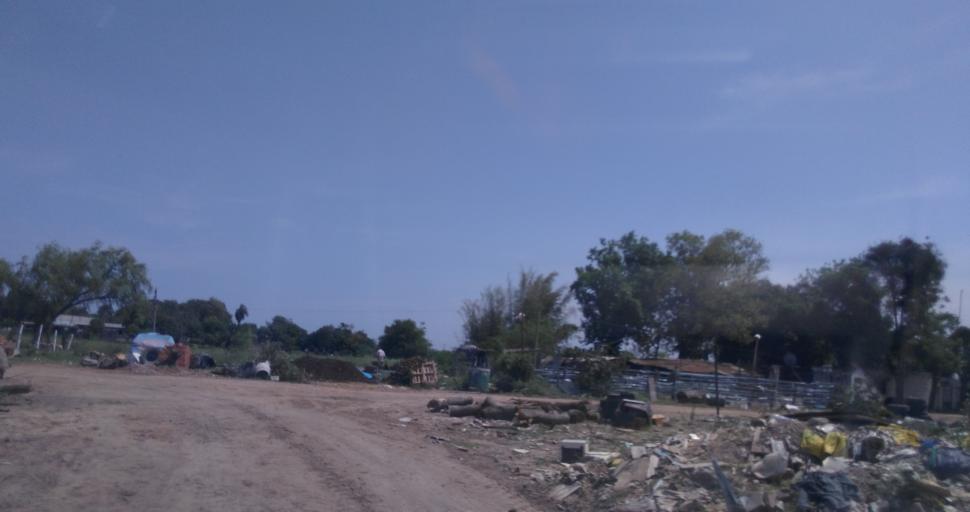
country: AR
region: Chaco
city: Fontana
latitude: -27.4195
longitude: -59.0147
